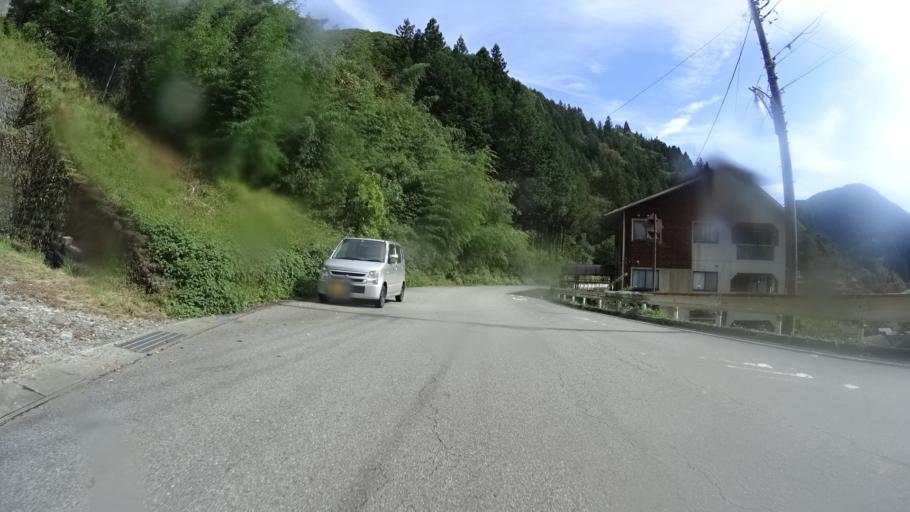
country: JP
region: Yamanashi
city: Otsuki
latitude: 35.7943
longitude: 138.9131
